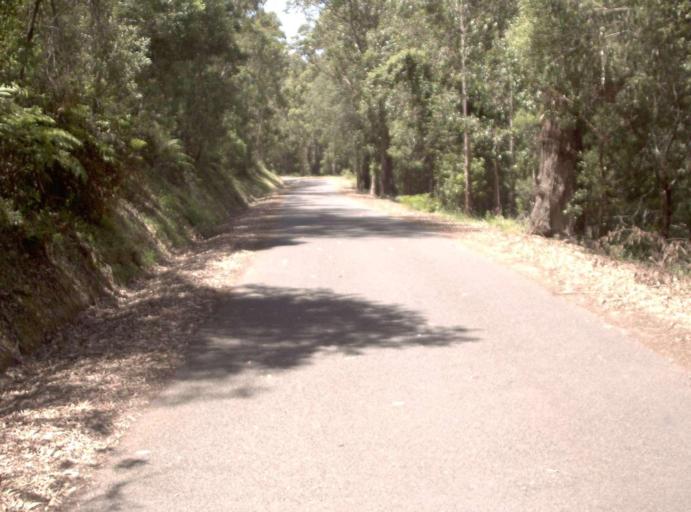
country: AU
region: New South Wales
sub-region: Bombala
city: Bombala
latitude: -37.4643
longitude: 148.9369
